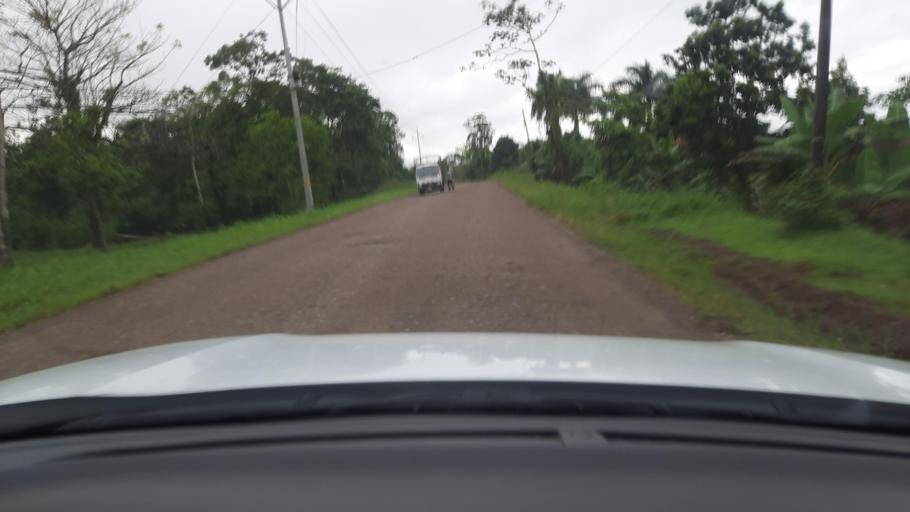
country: CR
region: Alajuela
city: San Jose
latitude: 11.0025
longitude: -85.3087
